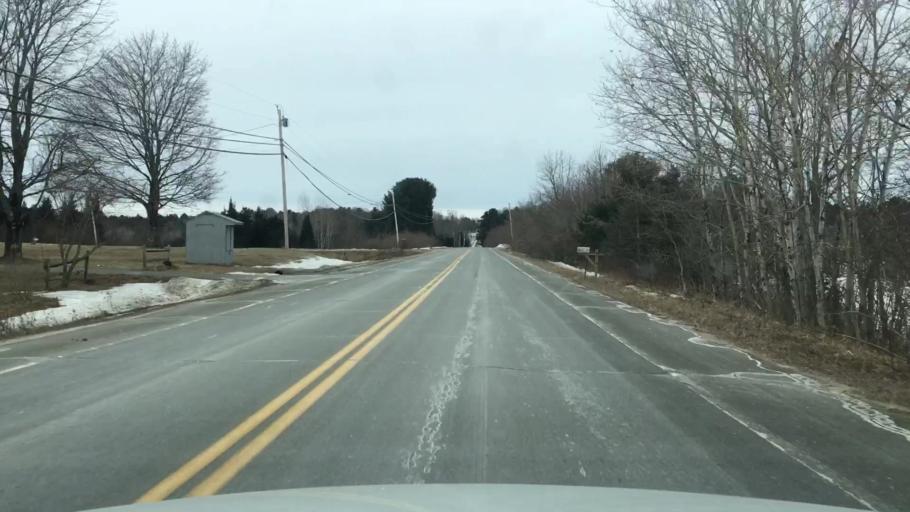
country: US
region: Maine
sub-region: Lincoln County
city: Whitefield
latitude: 44.2244
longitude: -69.6049
